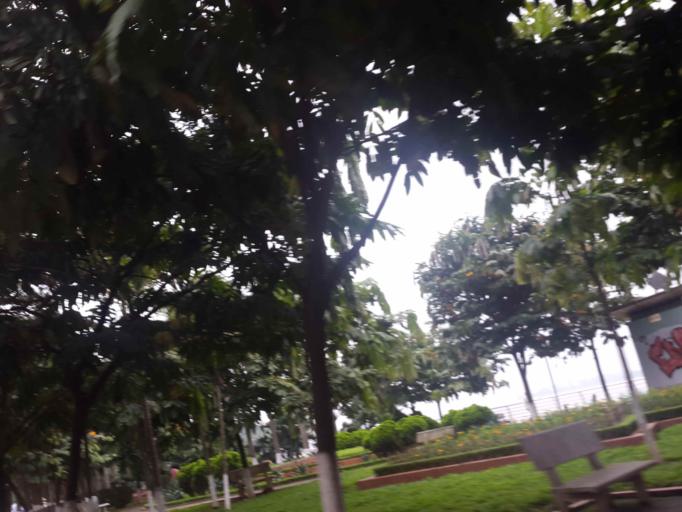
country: VN
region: Ha Noi
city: Cau Giay
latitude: 21.0456
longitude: 105.8152
